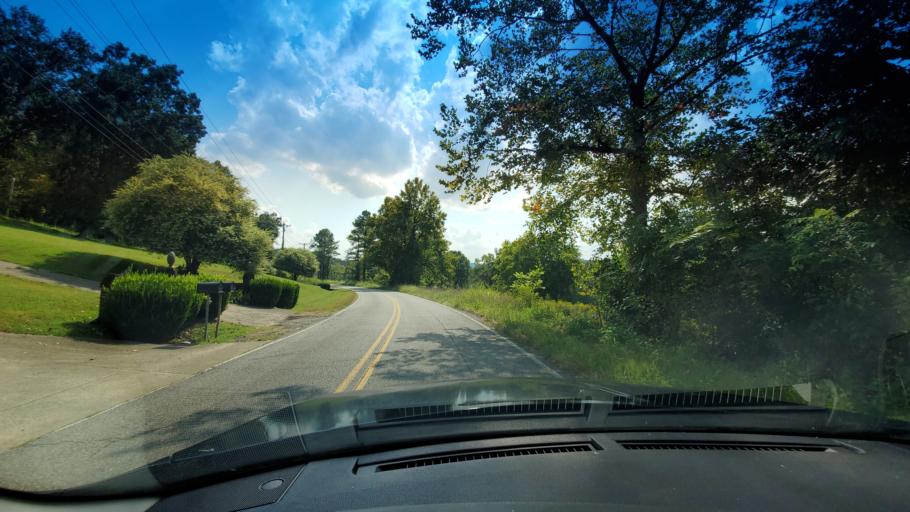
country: US
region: Tennessee
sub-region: Smith County
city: Carthage
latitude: 36.2509
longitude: -85.9657
